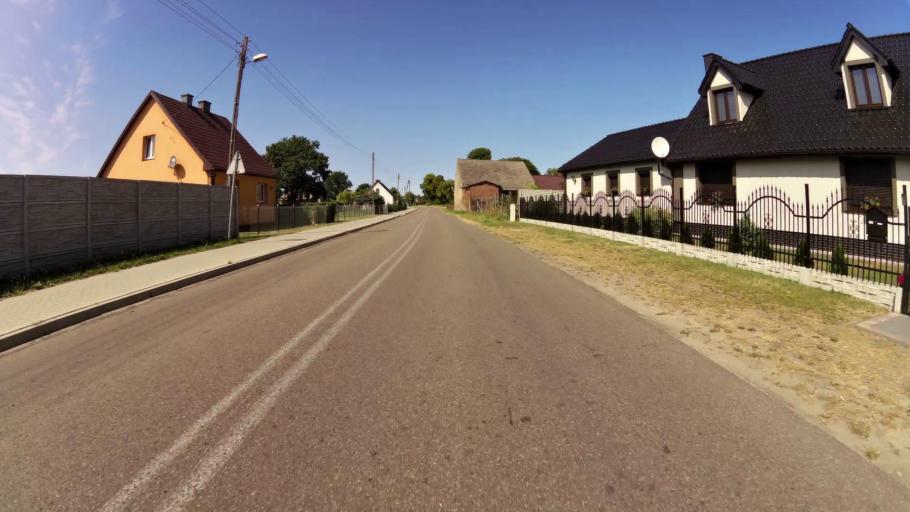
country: PL
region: West Pomeranian Voivodeship
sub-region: Powiat stargardzki
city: Dobrzany
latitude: 53.3421
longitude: 15.3956
